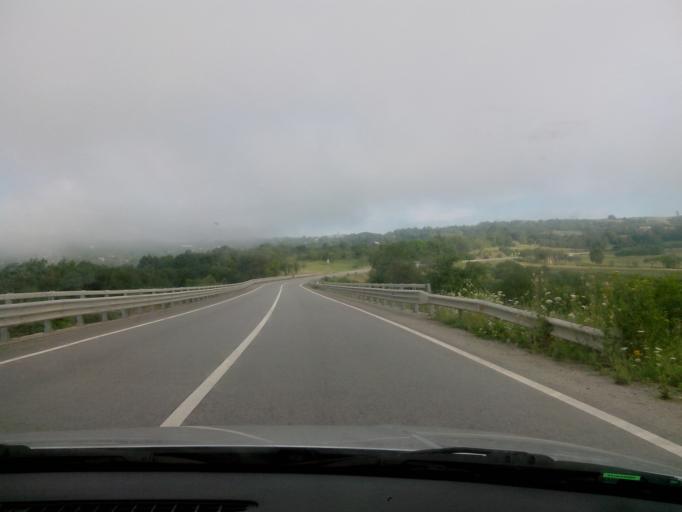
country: RO
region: Maramures
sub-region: Comuna Boiu Mare
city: Boiu Mare
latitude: 47.3721
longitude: 23.5366
